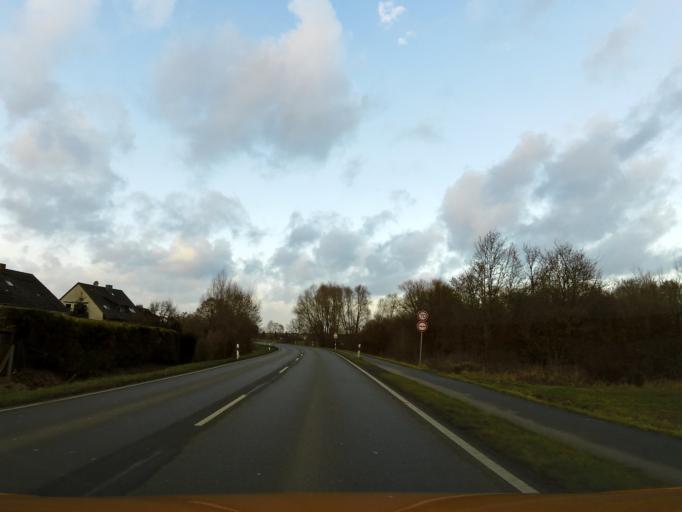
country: DE
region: Lower Saxony
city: Wolfsburg
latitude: 52.4003
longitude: 10.8374
